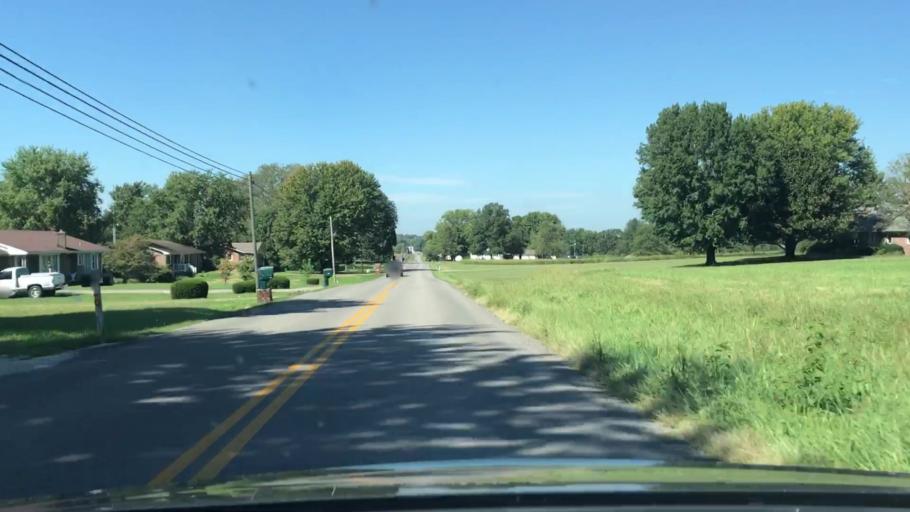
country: US
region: Kentucky
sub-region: Hardin County
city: Elizabethtown
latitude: 37.6020
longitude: -85.8891
